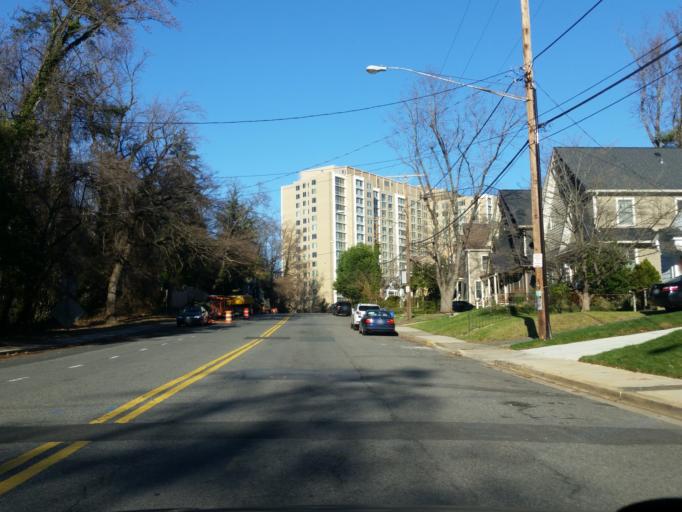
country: US
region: Maryland
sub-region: Montgomery County
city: Somerset
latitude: 38.9609
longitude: -77.0965
